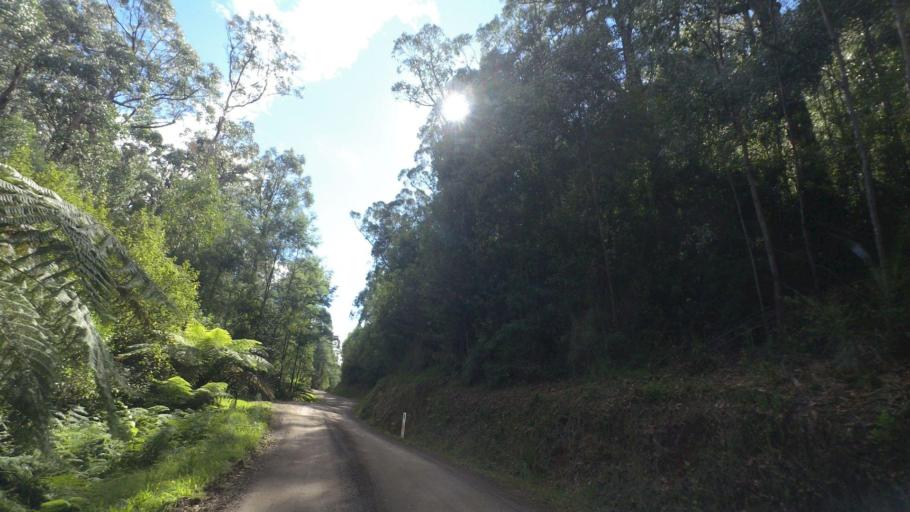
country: AU
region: Victoria
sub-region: Cardinia
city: Bunyip
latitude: -37.9687
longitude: 145.8158
